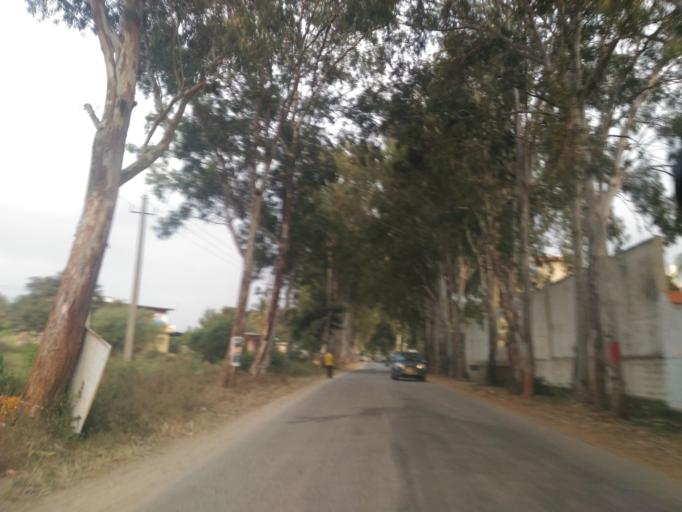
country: IN
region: Karnataka
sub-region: Chikkaballapur
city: Chik Ballapur
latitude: 13.3479
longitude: 77.6847
